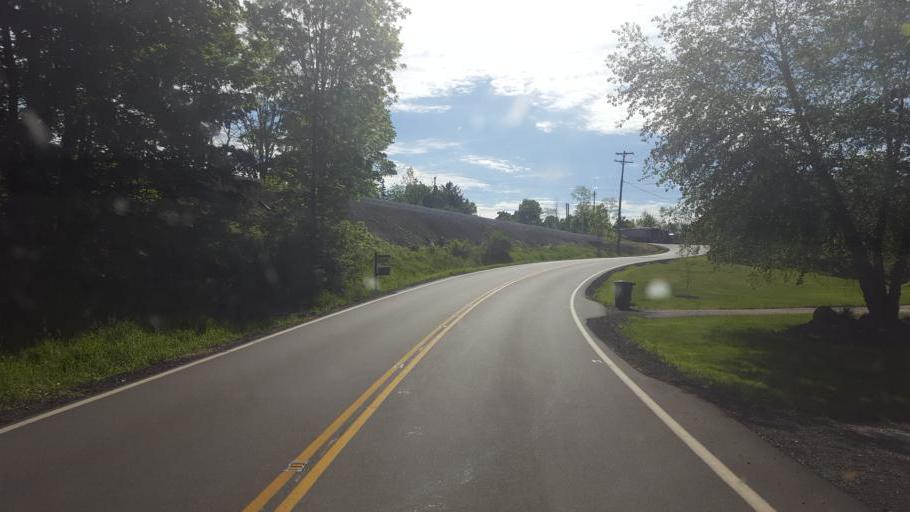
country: US
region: Ohio
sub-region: Medina County
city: Wadsworth
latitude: 41.0994
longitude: -81.7776
